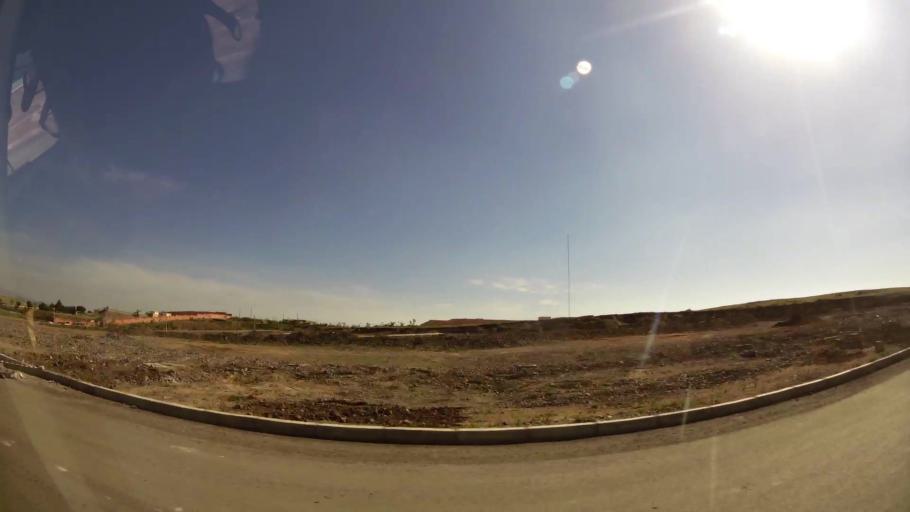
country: MA
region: Oriental
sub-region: Oujda-Angad
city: Oujda
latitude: 34.6482
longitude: -1.9523
